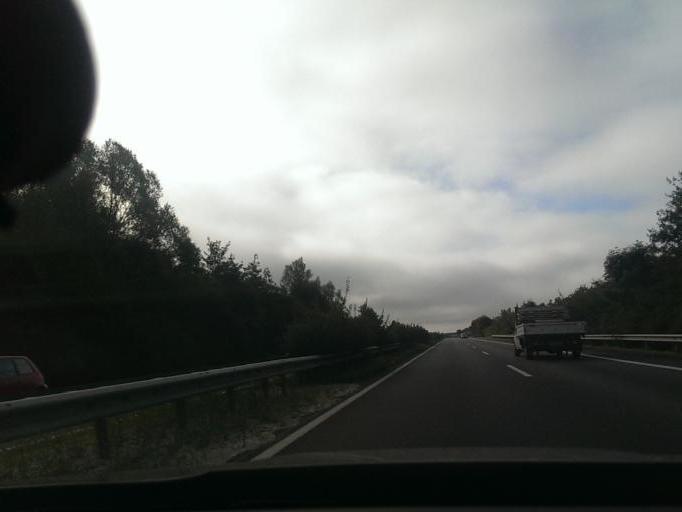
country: DE
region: Lower Saxony
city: Flothe
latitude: 52.1007
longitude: 10.4914
